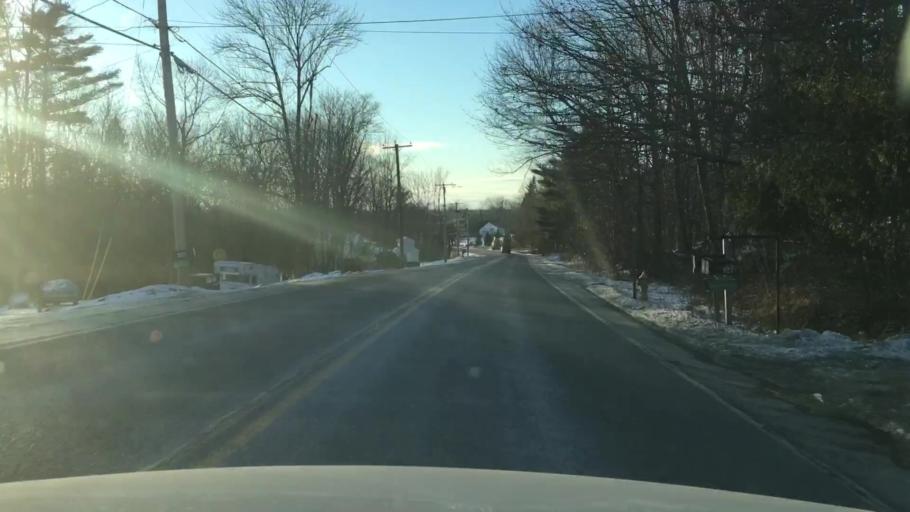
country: US
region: Maine
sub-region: Penobscot County
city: Eddington
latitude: 44.8299
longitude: -68.6692
